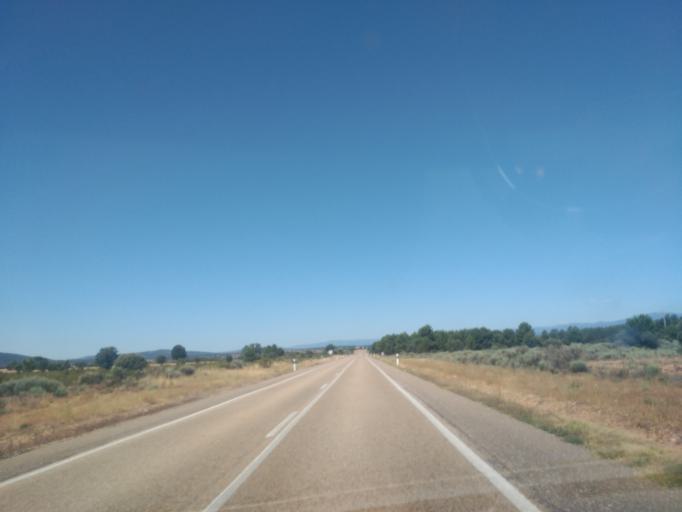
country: ES
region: Castille and Leon
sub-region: Provincia de Zamora
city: Otero de Bodas
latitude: 41.9403
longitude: -6.1726
